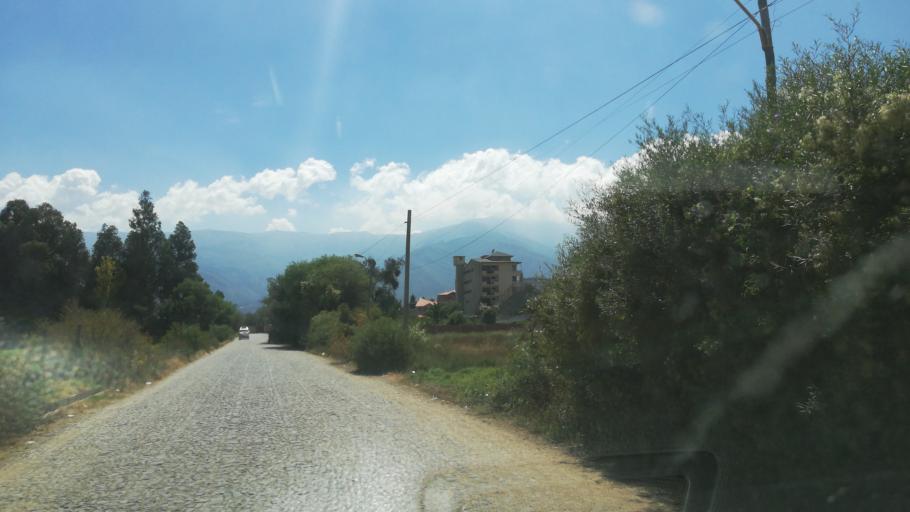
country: BO
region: Cochabamba
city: Cochabamba
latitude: -17.3710
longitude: -66.2100
